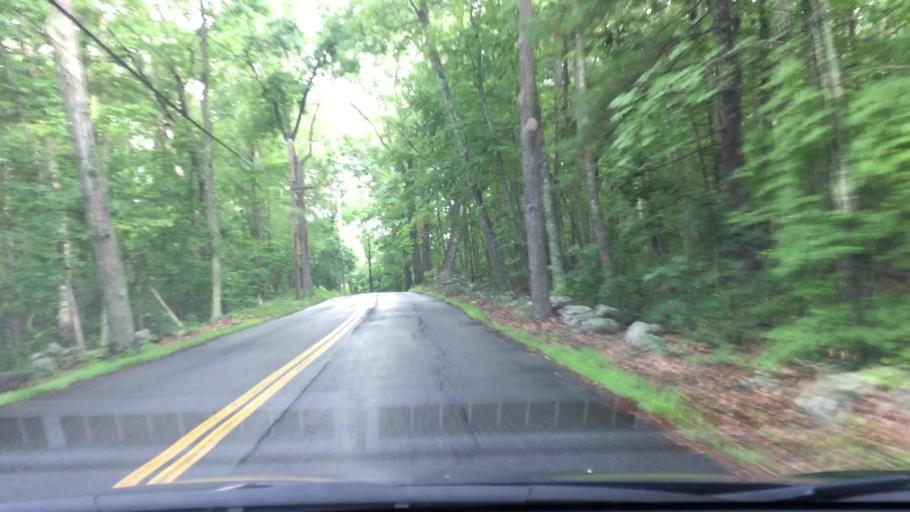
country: US
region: Massachusetts
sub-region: Middlesex County
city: Acton
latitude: 42.5041
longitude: -71.4439
